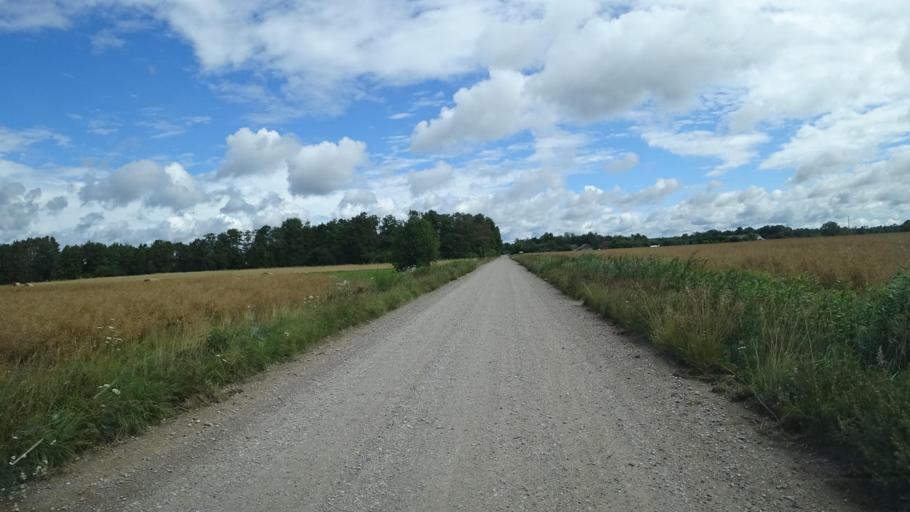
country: LV
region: Liepaja
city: Vec-Liepaja
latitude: 56.6589
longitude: 21.0659
